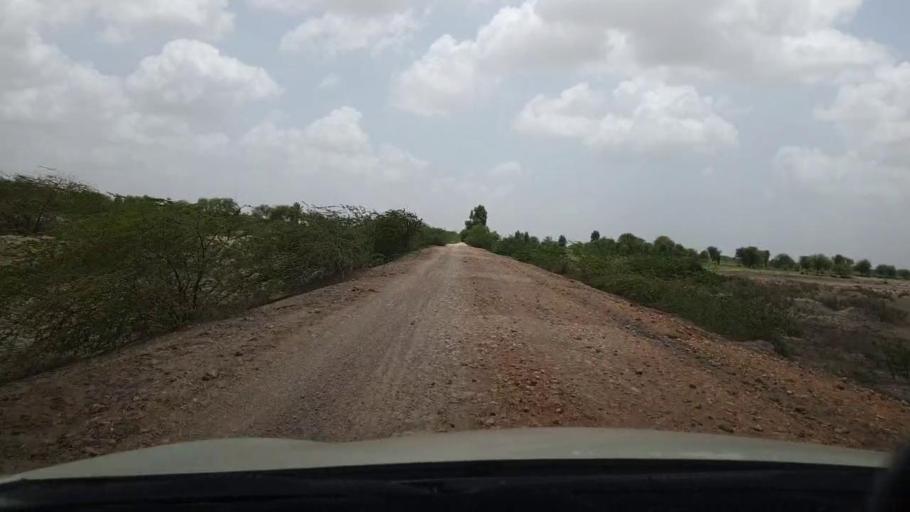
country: PK
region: Sindh
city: Kadhan
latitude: 24.3772
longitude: 68.9292
